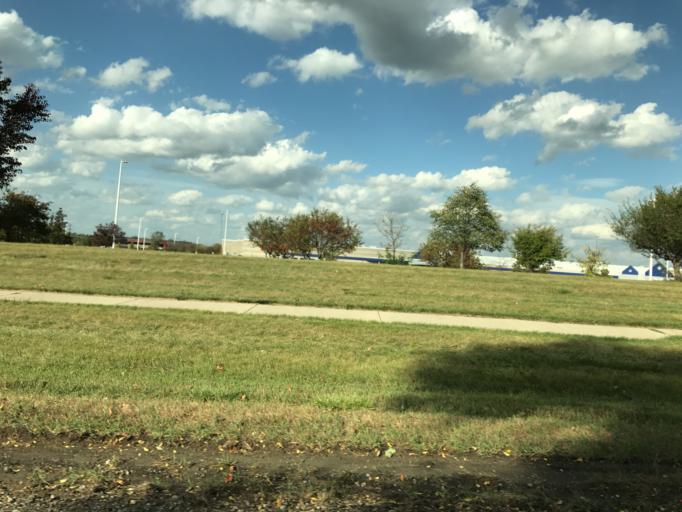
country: US
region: Michigan
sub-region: Oakland County
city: Wixom
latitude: 42.4957
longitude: -83.5424
